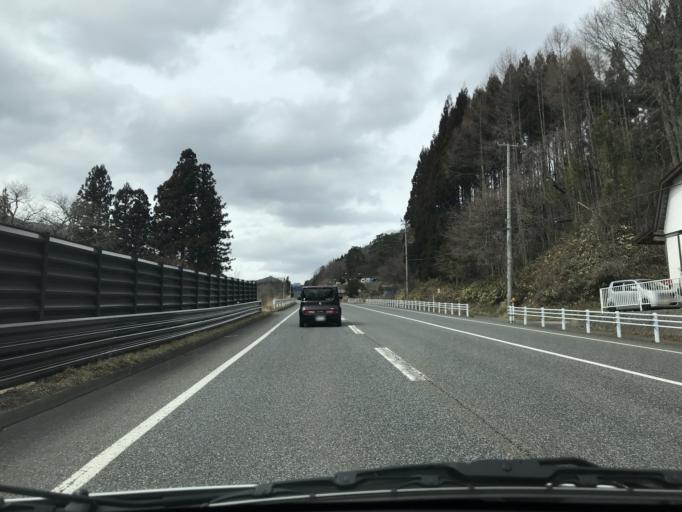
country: JP
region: Iwate
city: Tono
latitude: 39.3383
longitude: 141.4434
